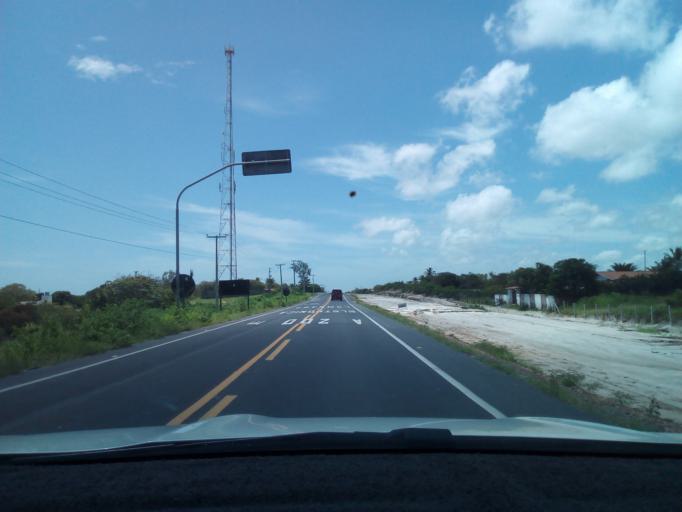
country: BR
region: Ceara
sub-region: Beberibe
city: Beberibe
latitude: -4.2688
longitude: -38.0535
